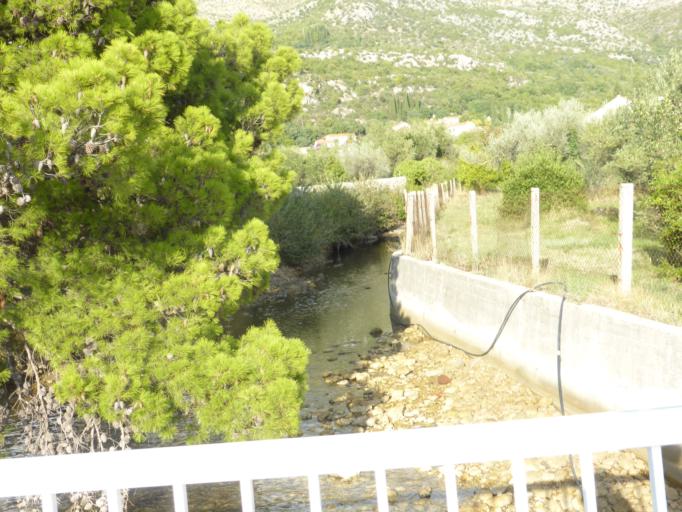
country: HR
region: Dubrovacko-Neretvanska
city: Podgora
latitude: 42.7840
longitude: 17.8890
